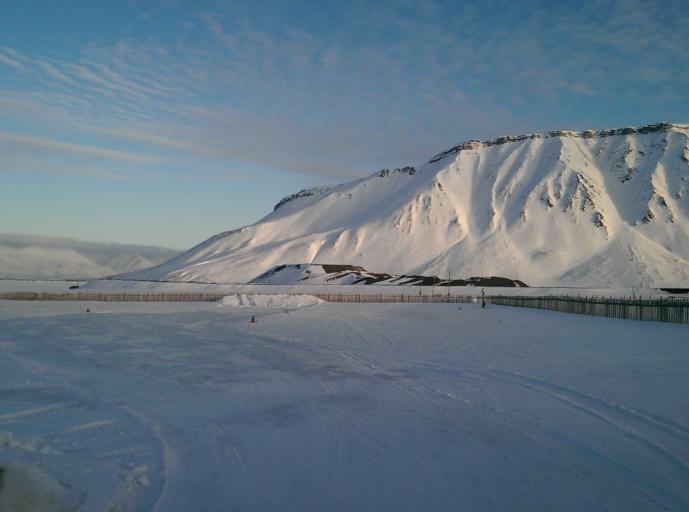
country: SJ
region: Svalbard
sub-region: Spitsbergen
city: Longyearbyen
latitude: 78.6528
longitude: 16.3365
